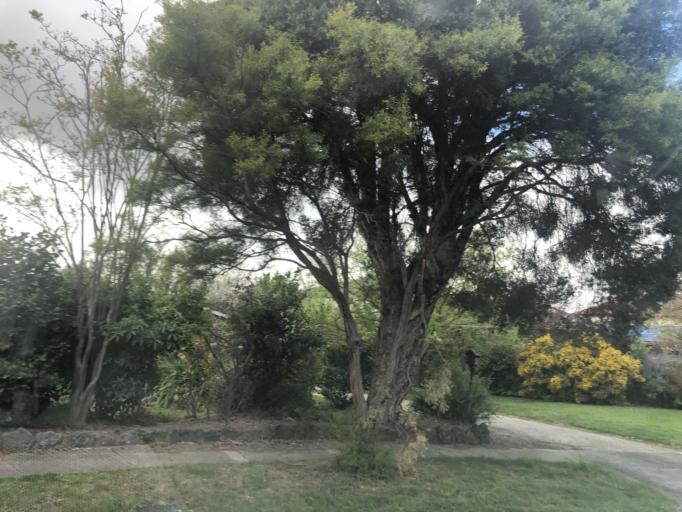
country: AU
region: Victoria
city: Burwood East
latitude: -37.8689
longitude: 145.1414
